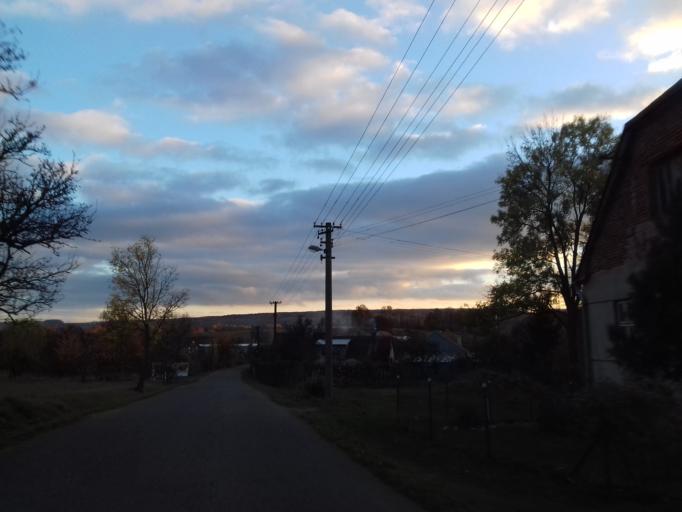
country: CZ
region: Pardubicky
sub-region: Okres Chrudim
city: Skutec
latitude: 49.8081
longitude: 15.9571
